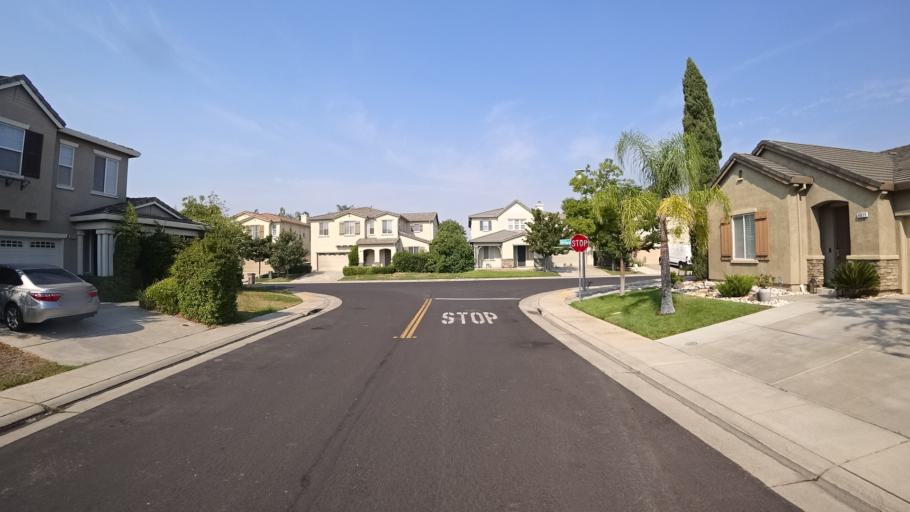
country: US
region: California
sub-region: Sacramento County
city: Laguna
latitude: 38.3835
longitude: -121.4260
